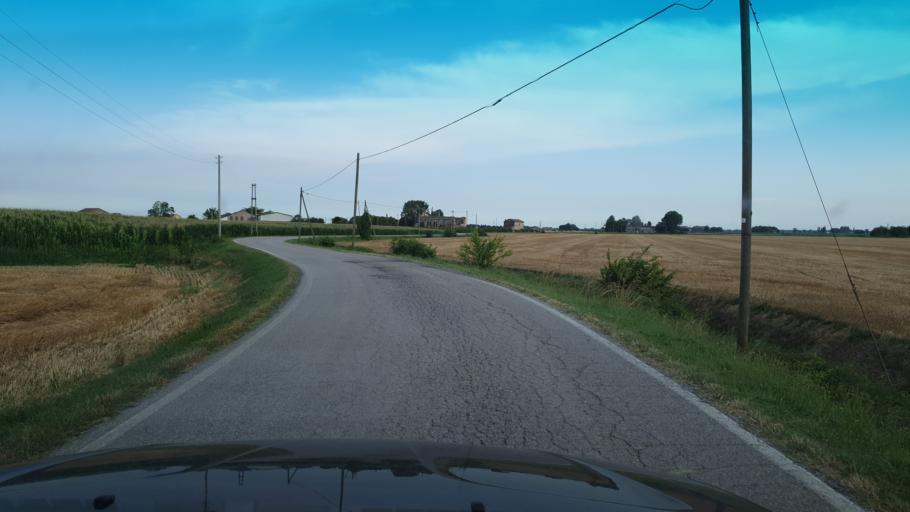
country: IT
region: Veneto
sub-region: Provincia di Rovigo
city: Castelguglielmo
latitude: 45.0056
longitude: 11.5281
